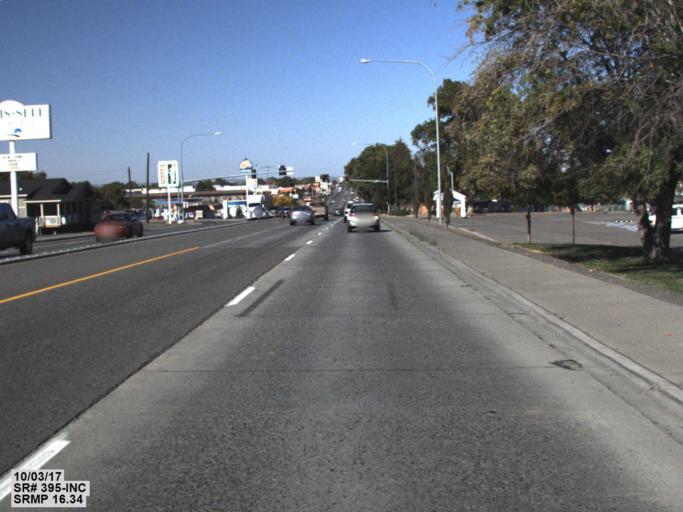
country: US
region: Washington
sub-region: Benton County
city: Kennewick
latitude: 46.2011
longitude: -119.1588
